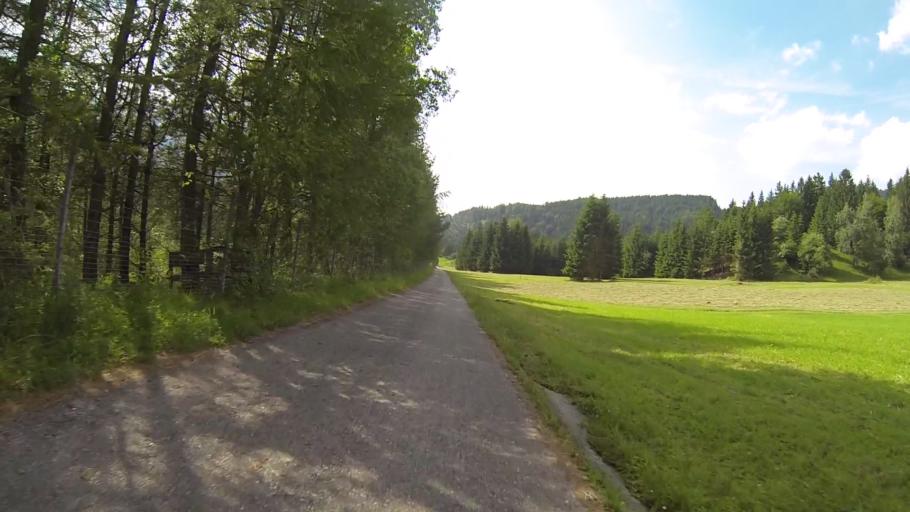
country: AT
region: Tyrol
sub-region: Politischer Bezirk Reutte
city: Pflach
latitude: 47.5174
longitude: 10.7269
